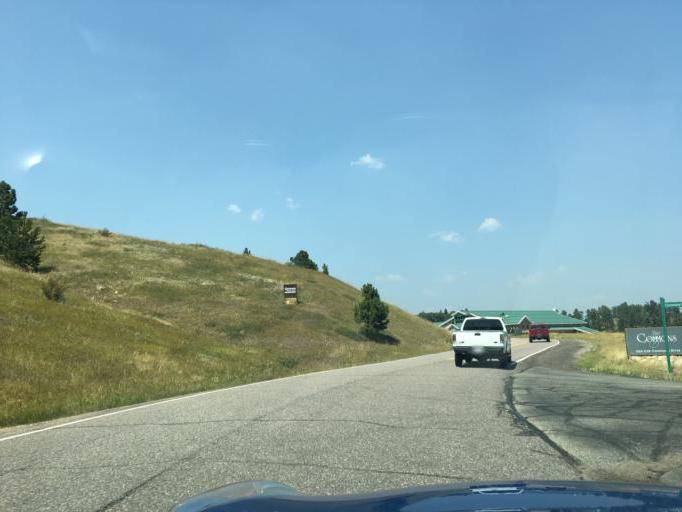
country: US
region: Colorado
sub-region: Jefferson County
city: Genesee
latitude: 39.7051
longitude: -105.2808
